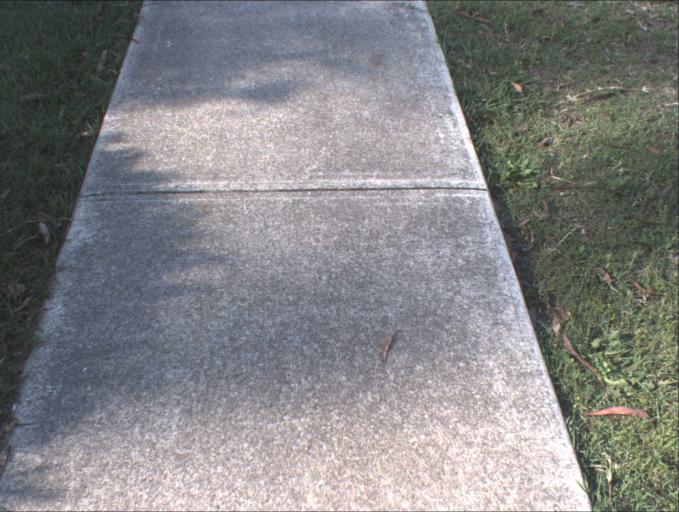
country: AU
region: Queensland
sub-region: Logan
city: Chambers Flat
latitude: -27.7691
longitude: 153.1071
